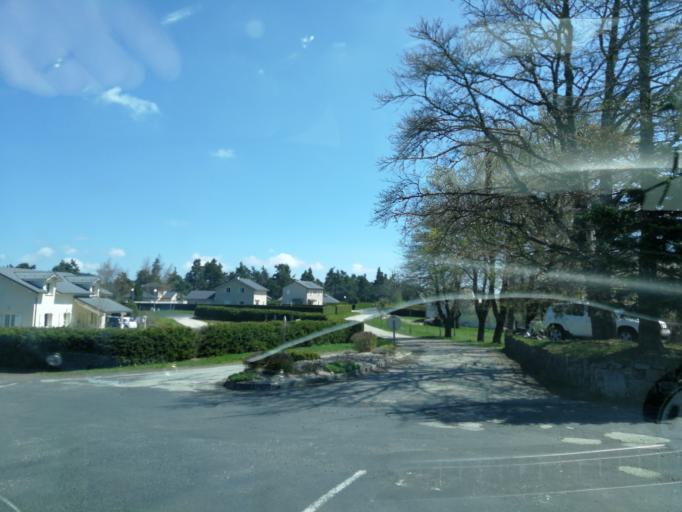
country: FR
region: Rhone-Alpes
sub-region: Departement de l'Ardeche
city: Saint-Agreve
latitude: 45.0145
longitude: 4.3982
